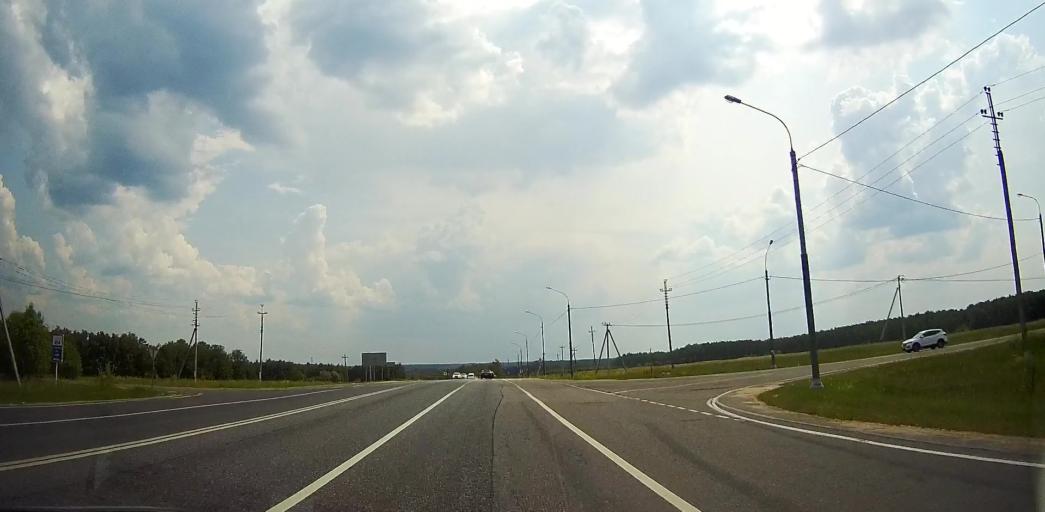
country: RU
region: Moskovskaya
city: Stupino
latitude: 54.9565
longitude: 38.1245
